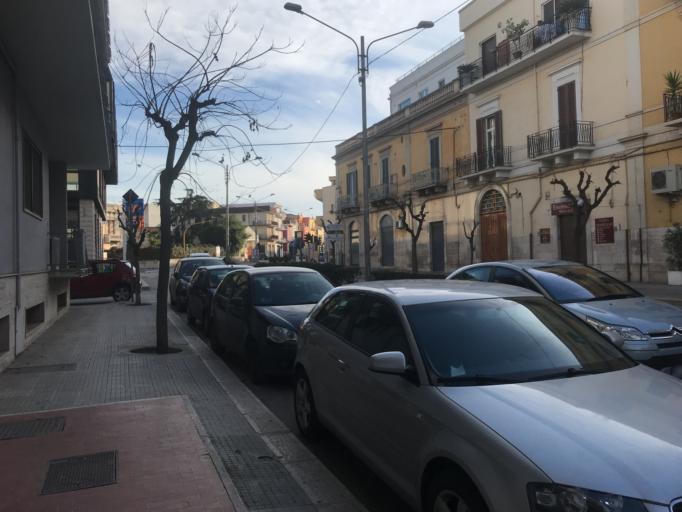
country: IT
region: Apulia
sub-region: Provincia di Bari
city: Corato
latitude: 41.1523
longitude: 16.4167
